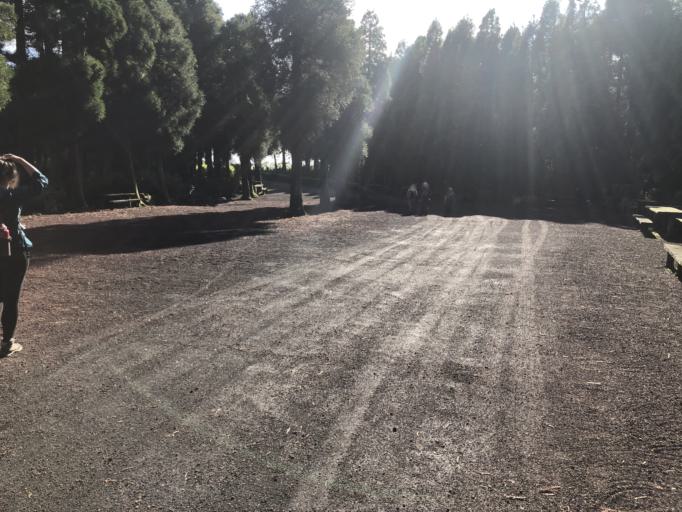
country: PT
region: Azores
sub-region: Ponta Delgada
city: Arrifes
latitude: 37.8383
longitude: -25.7583
